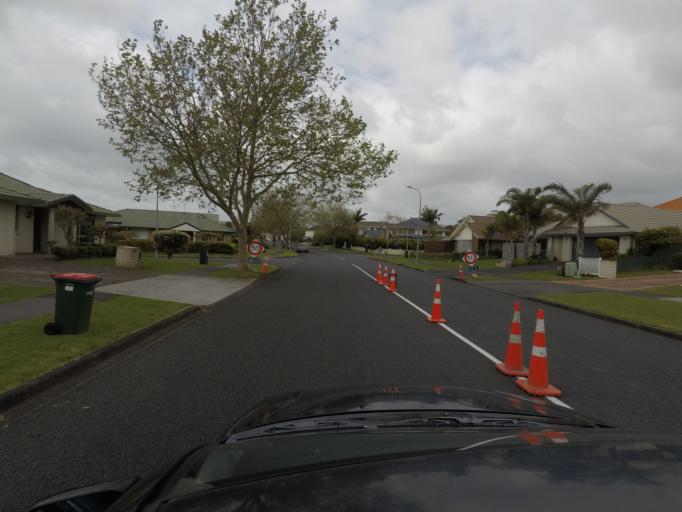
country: NZ
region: Auckland
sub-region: Auckland
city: Pakuranga
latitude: -36.9238
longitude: 174.9189
